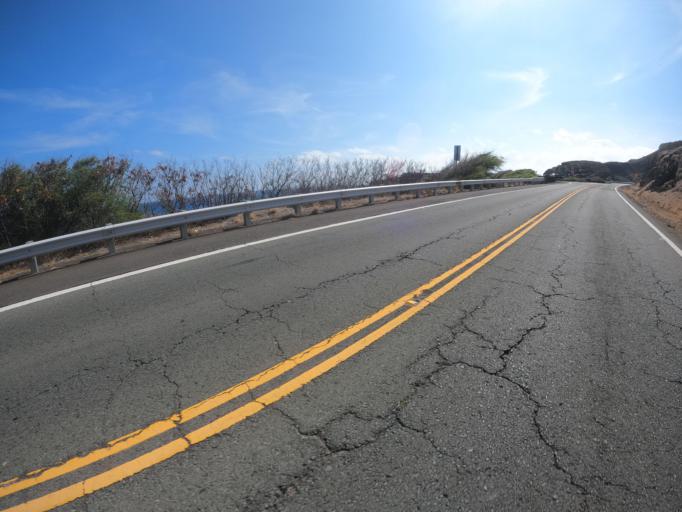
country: US
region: Hawaii
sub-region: Honolulu County
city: Waimanalo Beach
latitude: 21.2832
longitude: -157.6763
